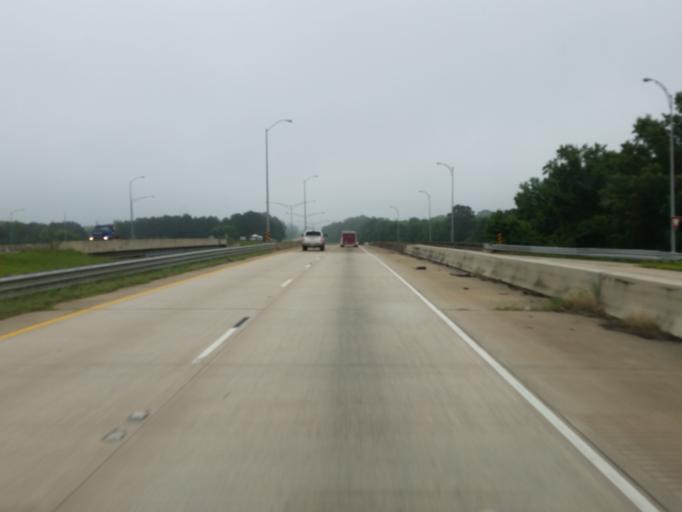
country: US
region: Louisiana
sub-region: Webster Parish
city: Minden
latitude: 32.5893
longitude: -93.2927
